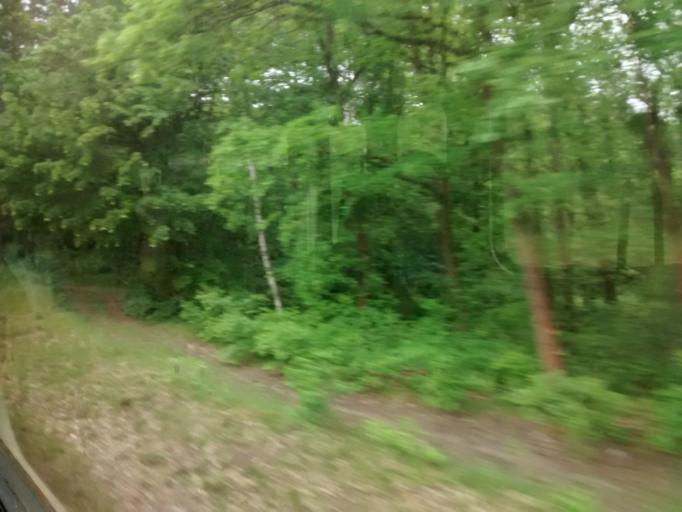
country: DE
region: Brandenburg
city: Birkenwerder
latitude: 52.6654
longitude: 13.3031
